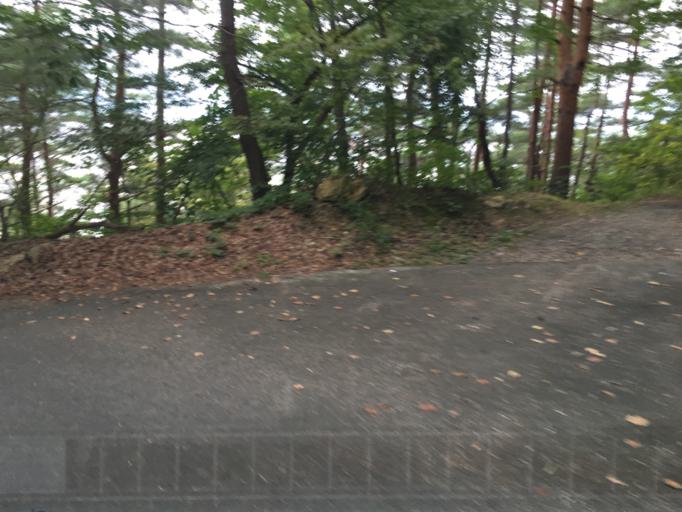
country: JP
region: Fukushima
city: Fukushima-shi
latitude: 37.7759
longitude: 140.4718
